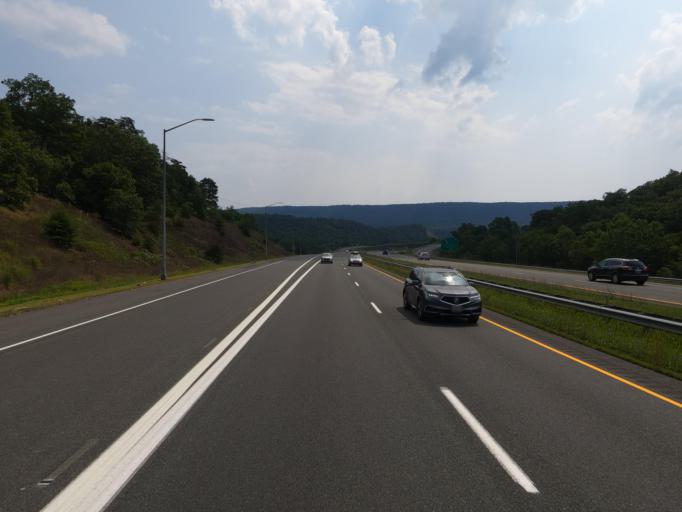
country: US
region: West Virginia
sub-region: Morgan County
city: Berkeley Springs
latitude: 39.7071
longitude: -78.3365
